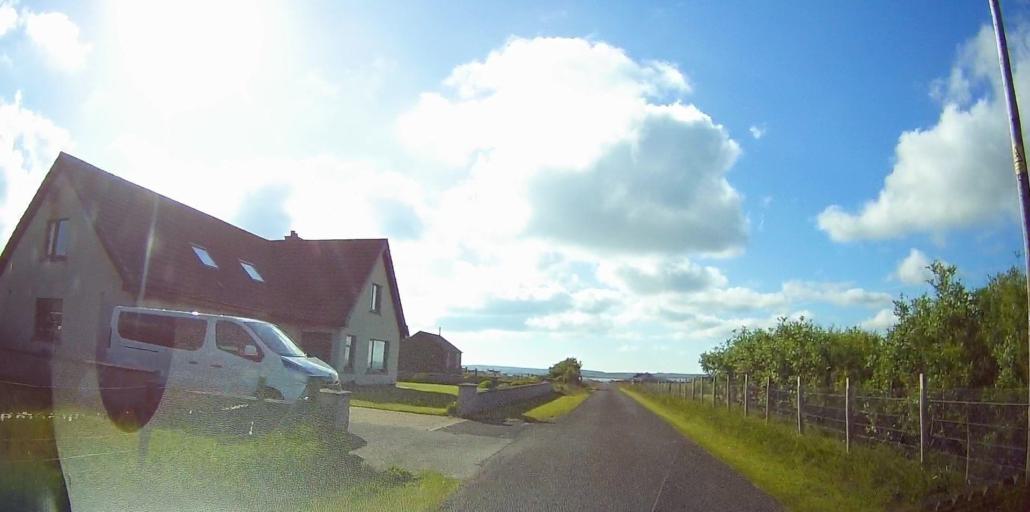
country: GB
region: Scotland
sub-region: Orkney Islands
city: Stromness
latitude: 58.9859
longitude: -3.1913
